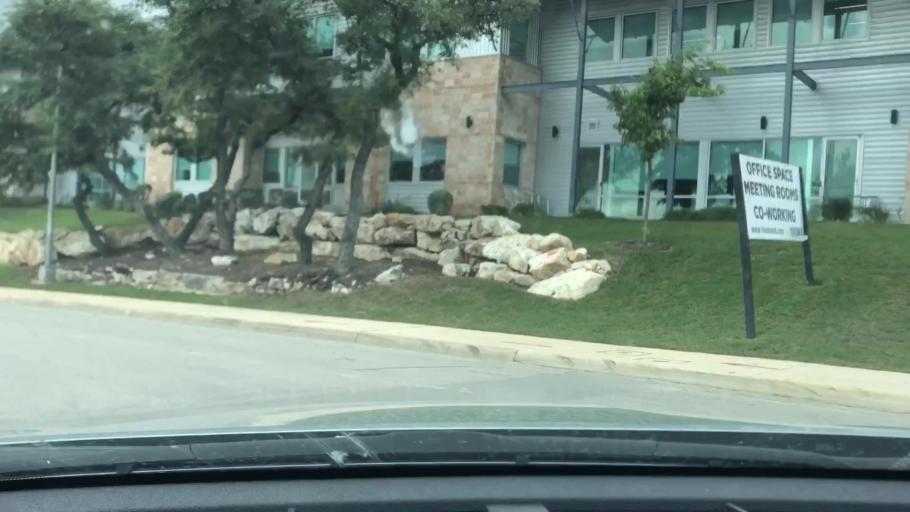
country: US
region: Texas
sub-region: Bexar County
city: Hollywood Park
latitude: 29.6185
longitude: -98.4763
